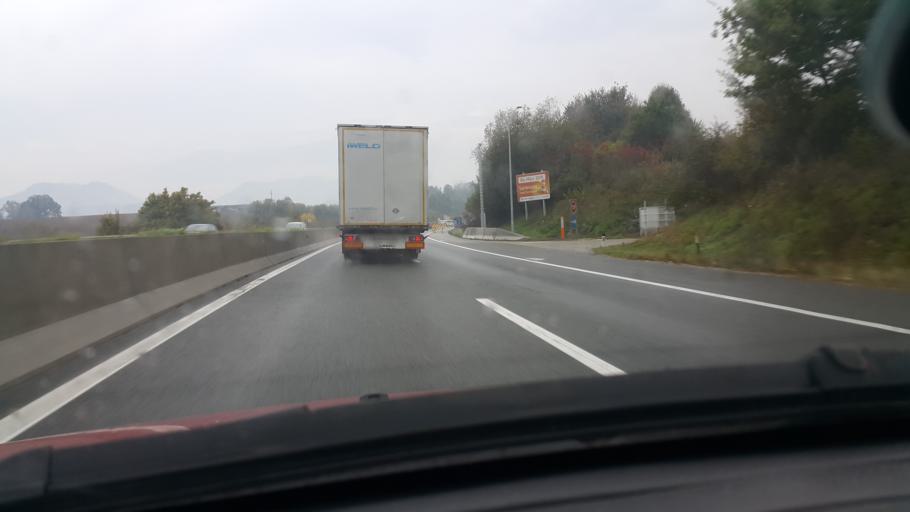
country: AT
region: Carinthia
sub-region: Politischer Bezirk Volkermarkt
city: Voelkermarkt
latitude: 46.6491
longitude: 14.5612
